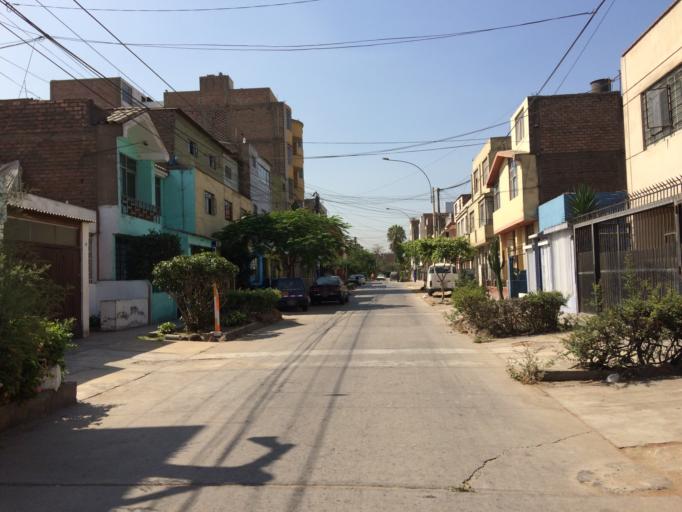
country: PE
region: Lima
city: Lima
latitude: -12.0252
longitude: -77.0384
